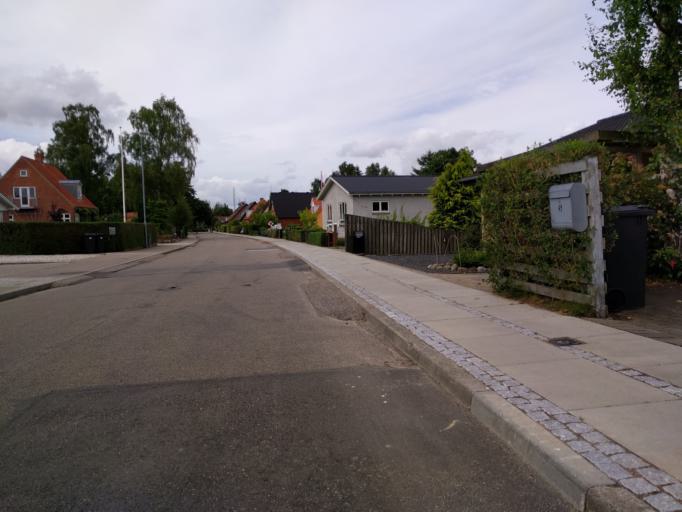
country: DK
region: Central Jutland
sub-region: Skanderborg Kommune
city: Ry
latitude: 56.0834
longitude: 9.7654
